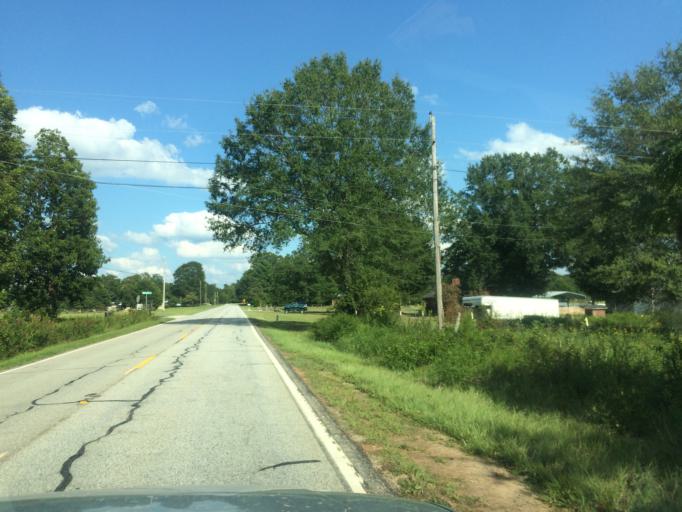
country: US
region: South Carolina
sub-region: Anderson County
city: Honea Path
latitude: 34.4521
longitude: -82.3600
